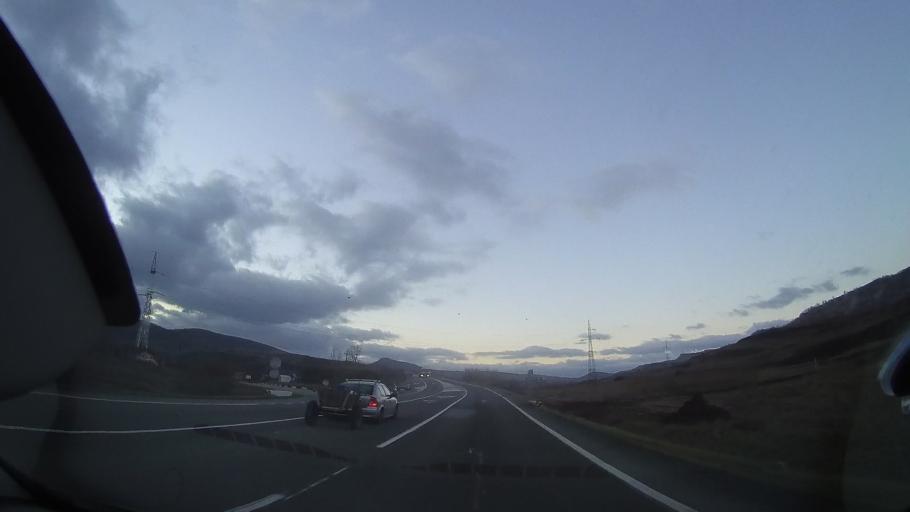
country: RO
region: Cluj
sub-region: Comuna Capusu Mare
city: Capusu Mare
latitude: 46.7992
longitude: 23.2713
